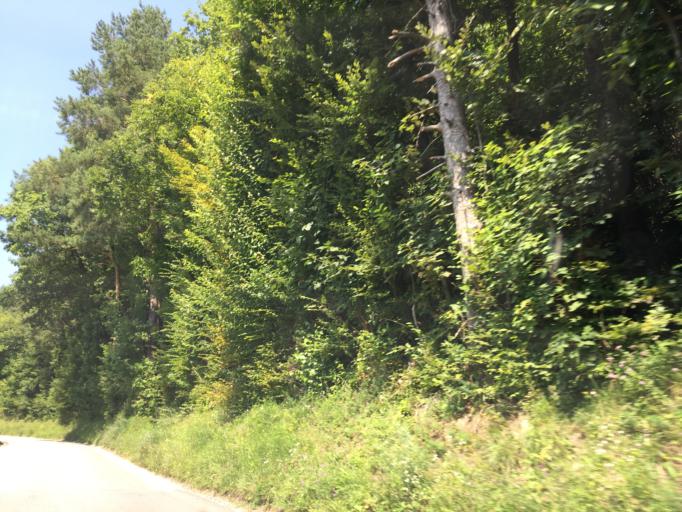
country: SI
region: Trbovlje
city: Trbovlje
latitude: 46.1763
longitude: 15.0513
